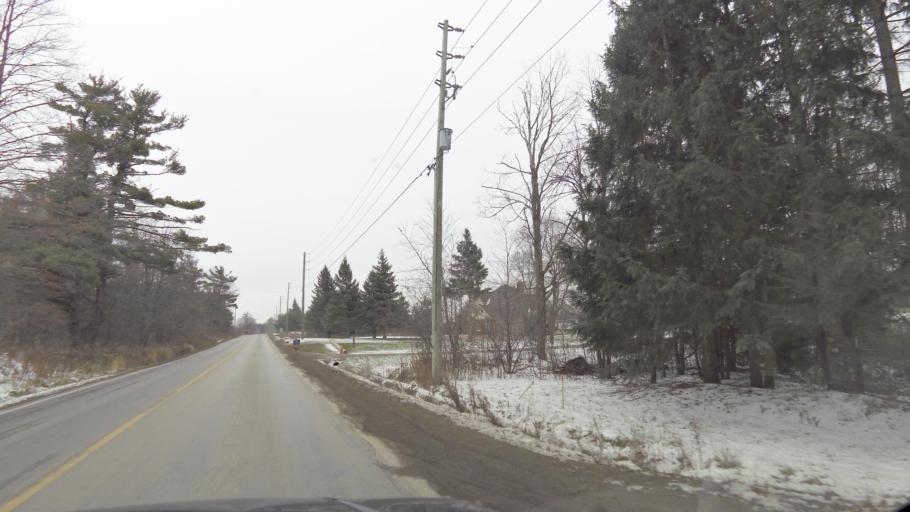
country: CA
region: Ontario
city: Vaughan
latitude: 43.8733
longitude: -79.6071
